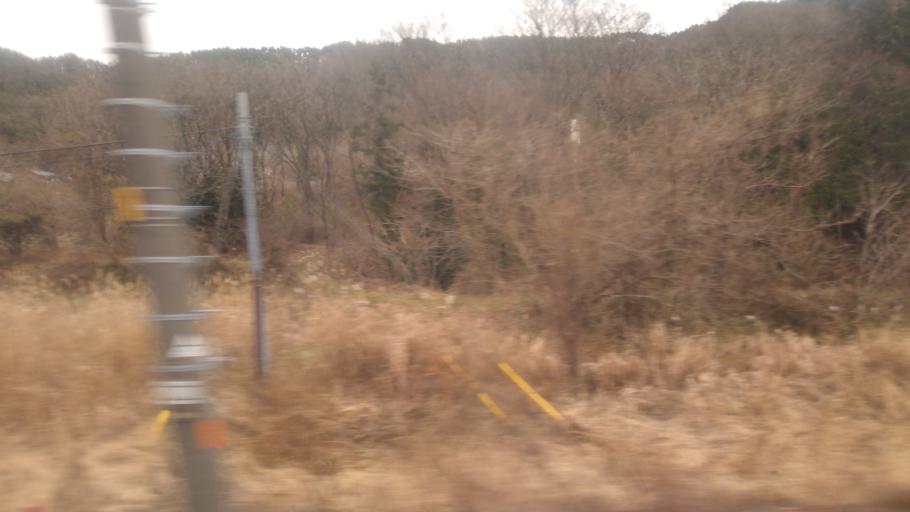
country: JP
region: Nagano
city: Ina
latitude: 35.8905
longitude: 137.7643
